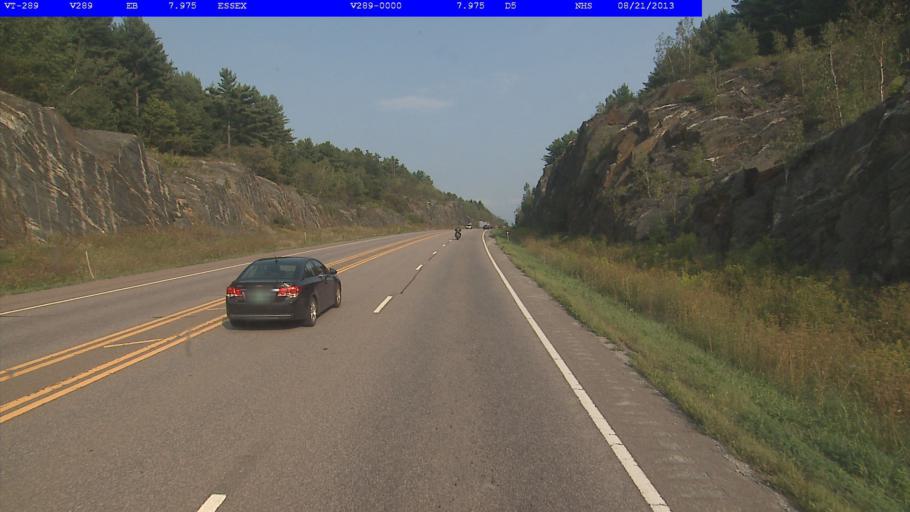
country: US
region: Vermont
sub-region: Chittenden County
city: Essex Junction
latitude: 44.5173
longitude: -73.1140
